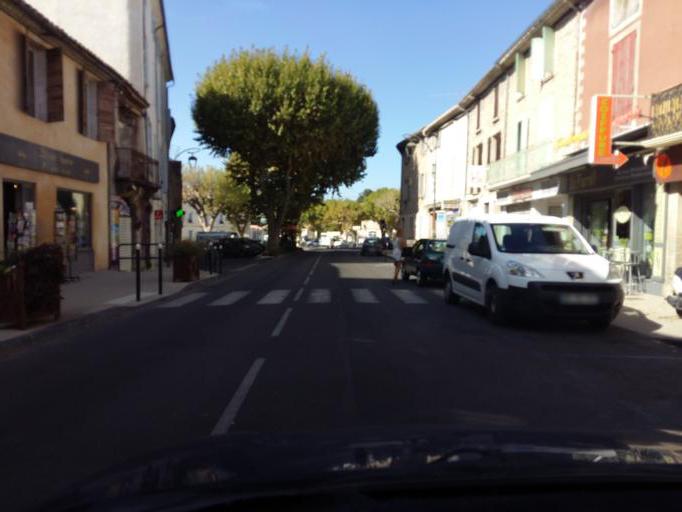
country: FR
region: Provence-Alpes-Cote d'Azur
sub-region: Departement du Vaucluse
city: Mazan
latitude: 44.0577
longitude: 5.1274
